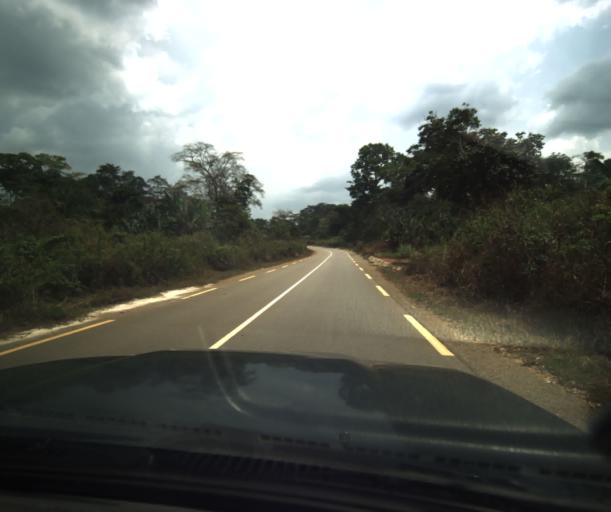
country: CM
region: Centre
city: Akono
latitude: 3.5334
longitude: 11.3118
